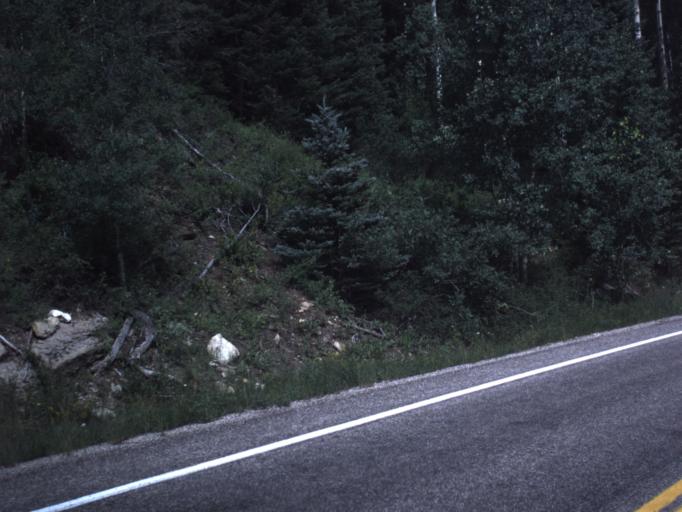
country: US
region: Utah
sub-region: Iron County
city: Cedar City
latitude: 37.6045
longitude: -112.9366
